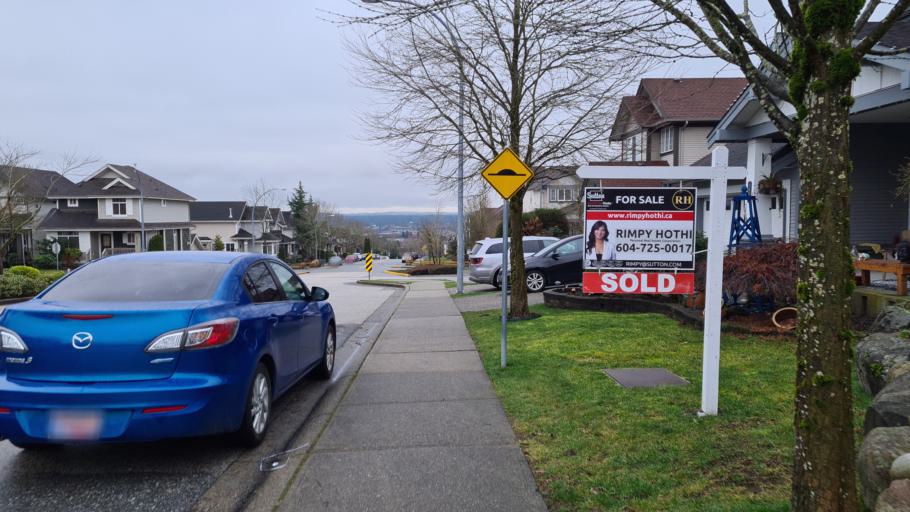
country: CA
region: British Columbia
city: Langley
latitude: 49.1308
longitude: -122.6648
